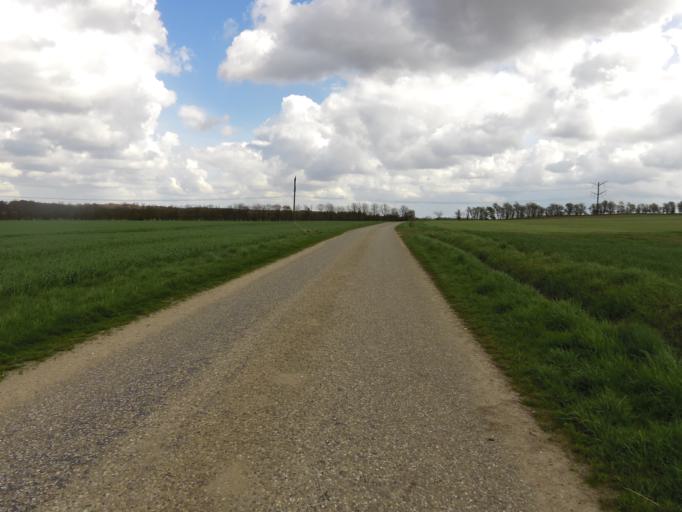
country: DK
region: South Denmark
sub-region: Tonder Kommune
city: Toftlund
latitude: 55.2150
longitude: 9.1414
